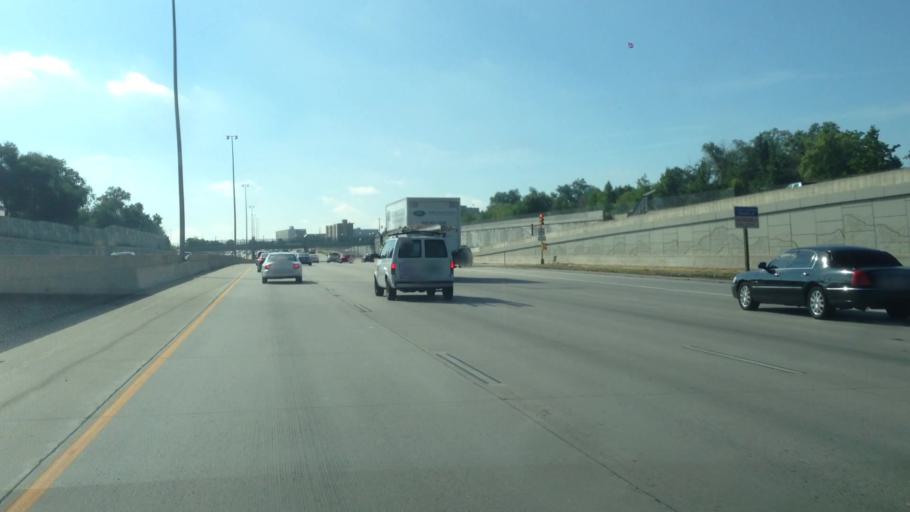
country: US
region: Colorado
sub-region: Arapahoe County
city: Glendale
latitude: 39.6882
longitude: -104.9719
